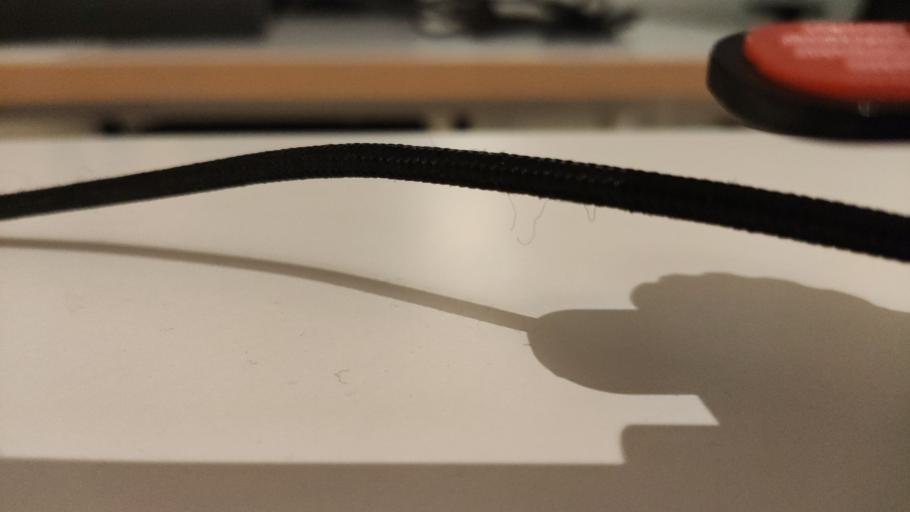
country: RU
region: Moskovskaya
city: Malaya Dubna
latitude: 55.8665
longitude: 38.9183
